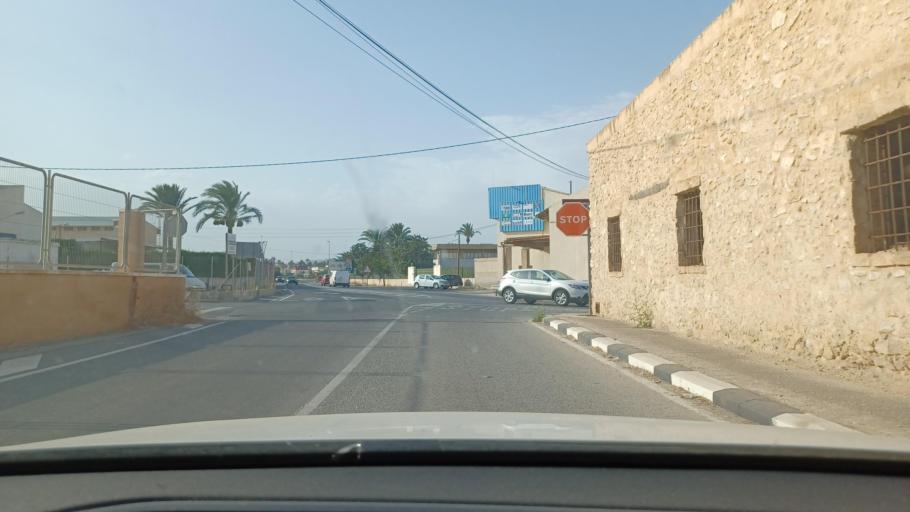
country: ES
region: Valencia
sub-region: Provincia de Alicante
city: Elche
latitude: 38.2500
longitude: -0.6915
